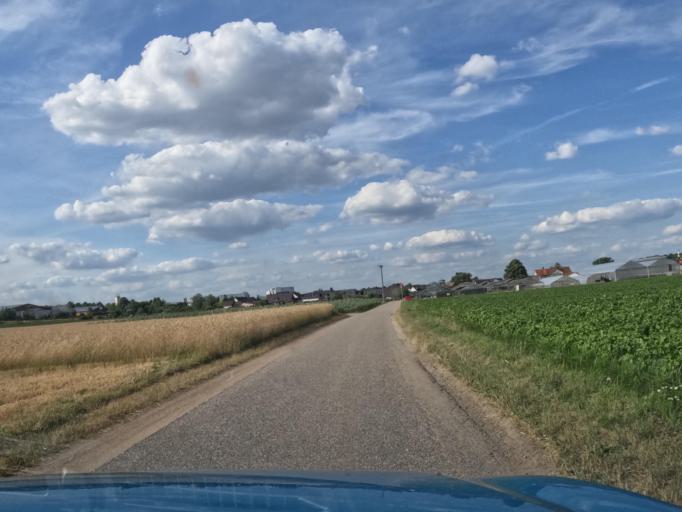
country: DE
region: Bavaria
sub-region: Upper Palatinate
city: Schwarzenfeld
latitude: 49.3807
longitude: 12.1209
